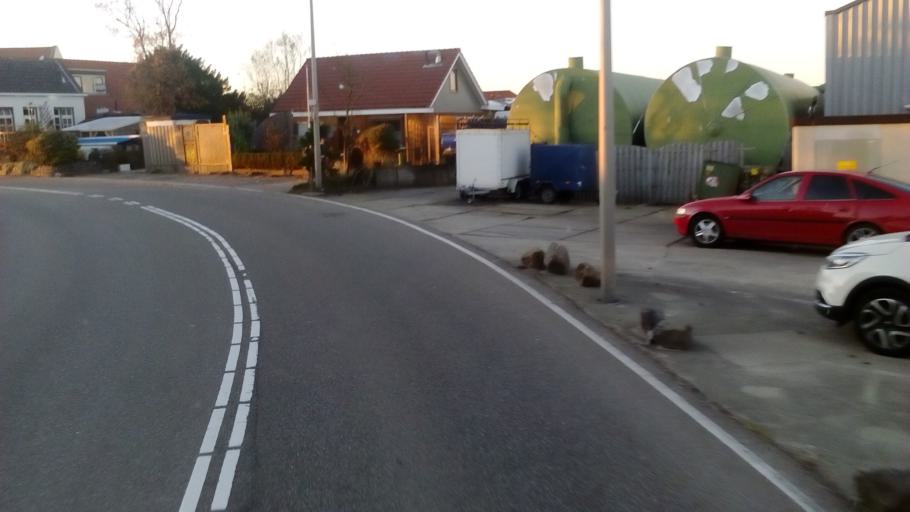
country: NL
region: South Holland
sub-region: Gemeente Westland
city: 's-Gravenzande
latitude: 52.0040
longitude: 4.1855
